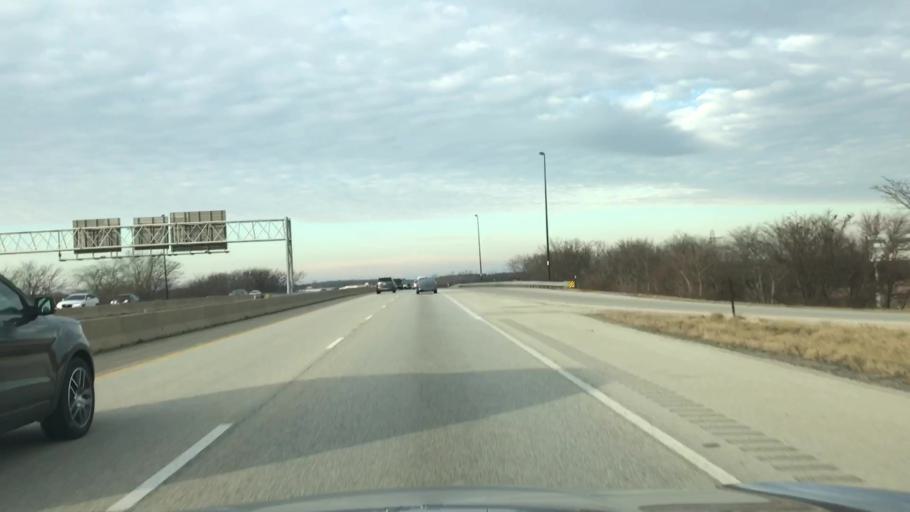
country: US
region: Illinois
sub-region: Sangamon County
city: Grandview
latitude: 39.8340
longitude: -89.5930
